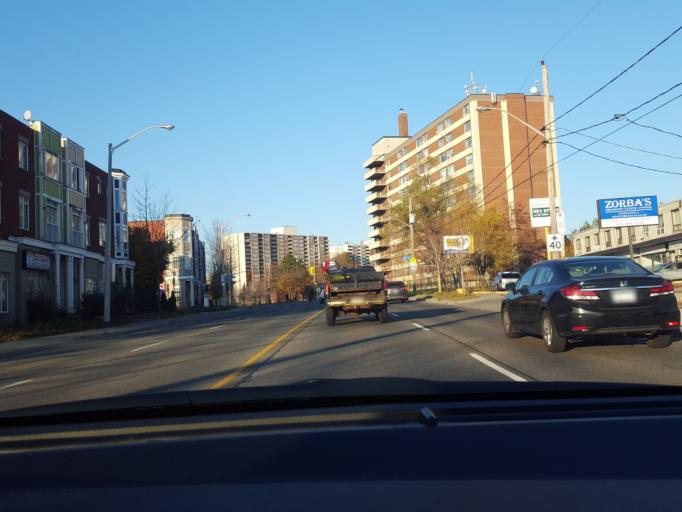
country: CA
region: Ontario
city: Scarborough
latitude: 43.7147
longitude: -79.3056
